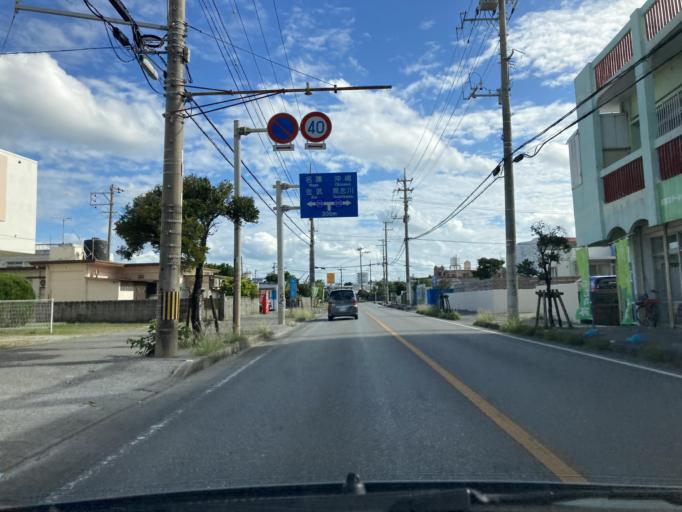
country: JP
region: Okinawa
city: Ishikawa
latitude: 26.4125
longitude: 127.8246
